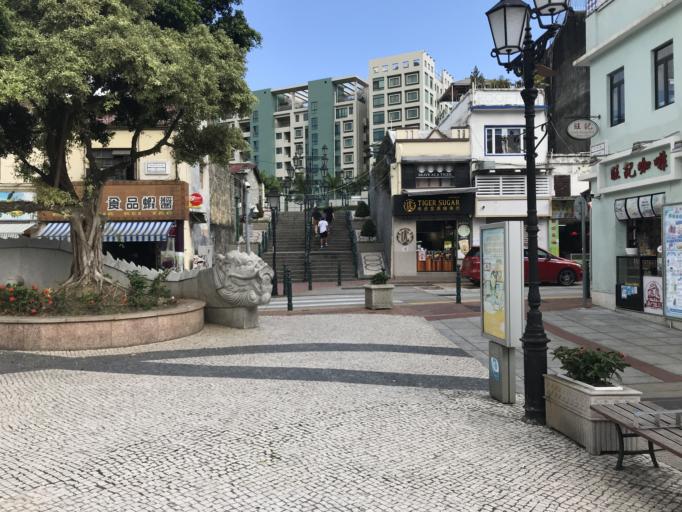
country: MO
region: Macau
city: Macau
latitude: 22.1533
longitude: 113.5572
